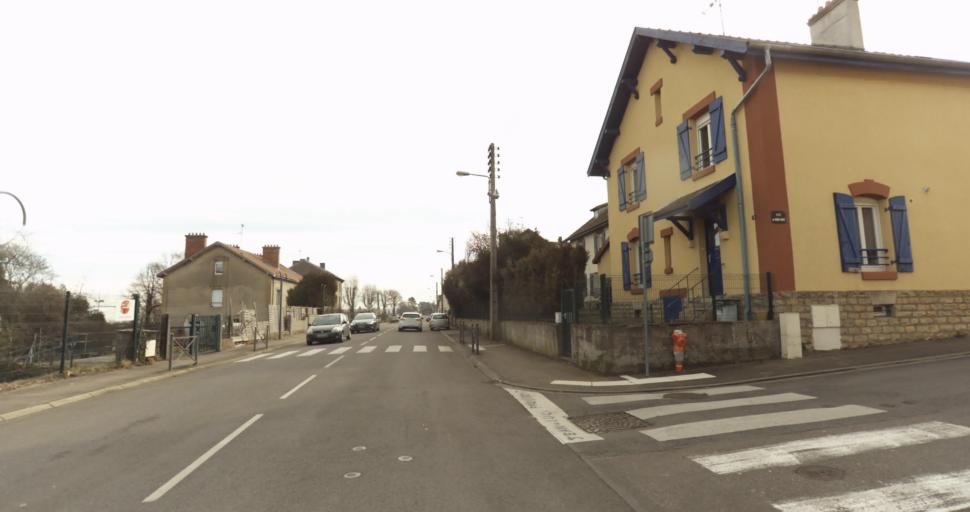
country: FR
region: Lorraine
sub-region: Departement de Meurthe-et-Moselle
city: Labry
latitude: 49.1650
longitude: 5.8723
